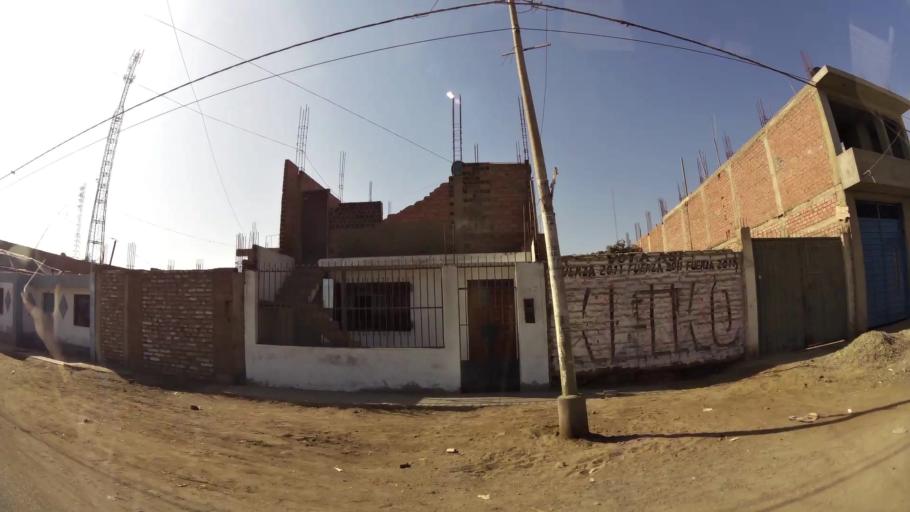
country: PE
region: Ica
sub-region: Provincia de Chincha
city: Chincha Alta
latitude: -13.3986
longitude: -76.1259
